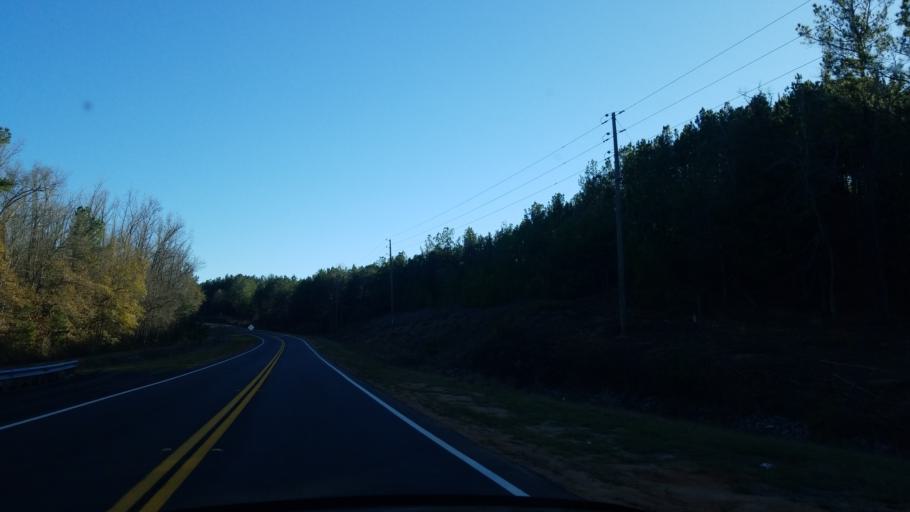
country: US
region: Georgia
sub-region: Talbot County
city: Talbotton
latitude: 32.5492
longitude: -84.5330
